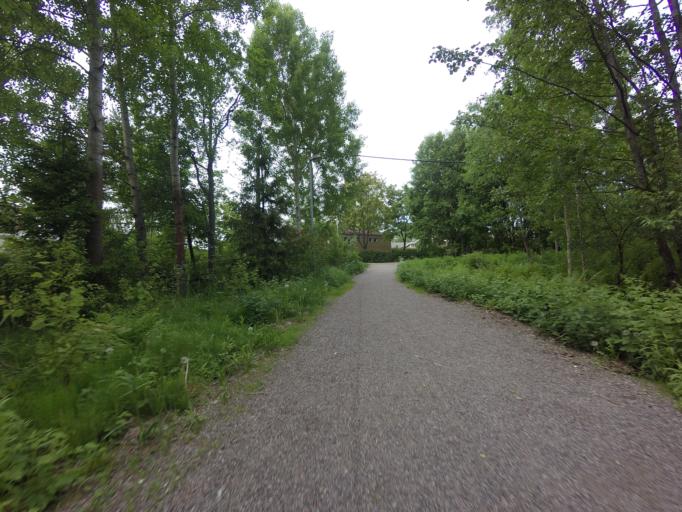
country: FI
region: Uusimaa
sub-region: Helsinki
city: Koukkuniemi
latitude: 60.1588
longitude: 24.7293
